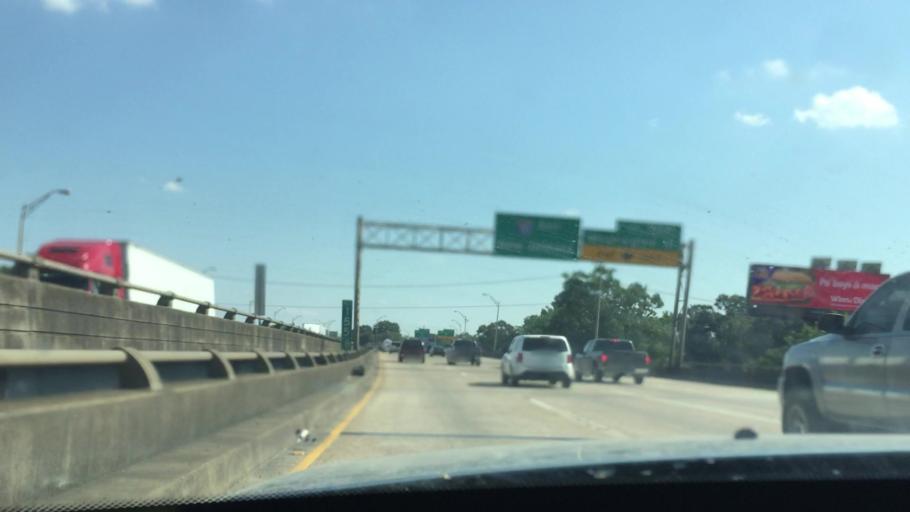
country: US
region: Louisiana
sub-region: East Baton Rouge Parish
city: Baton Rouge
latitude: 30.4353
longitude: -91.1774
